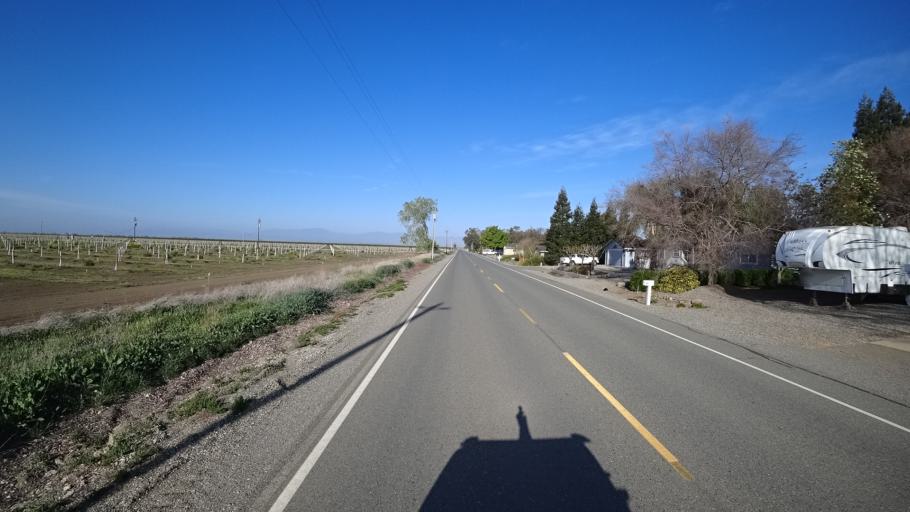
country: US
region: California
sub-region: Glenn County
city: Willows
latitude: 39.5824
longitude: -122.2200
